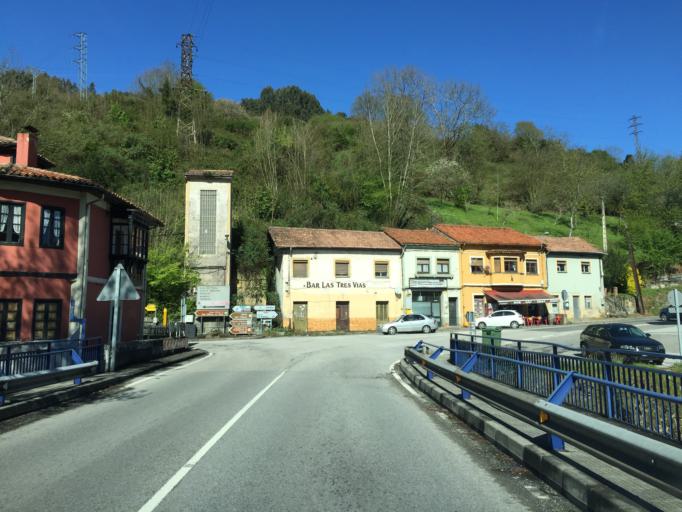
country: ES
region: Asturias
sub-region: Province of Asturias
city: Castandiello
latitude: 43.3540
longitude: -5.9660
